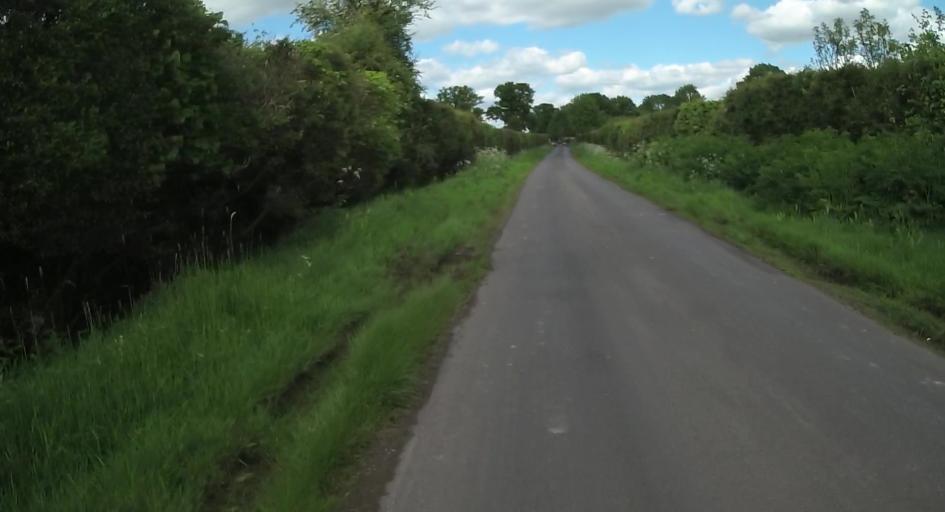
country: GB
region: England
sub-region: West Berkshire
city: Stratfield Mortimer
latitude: 51.3393
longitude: -1.0423
